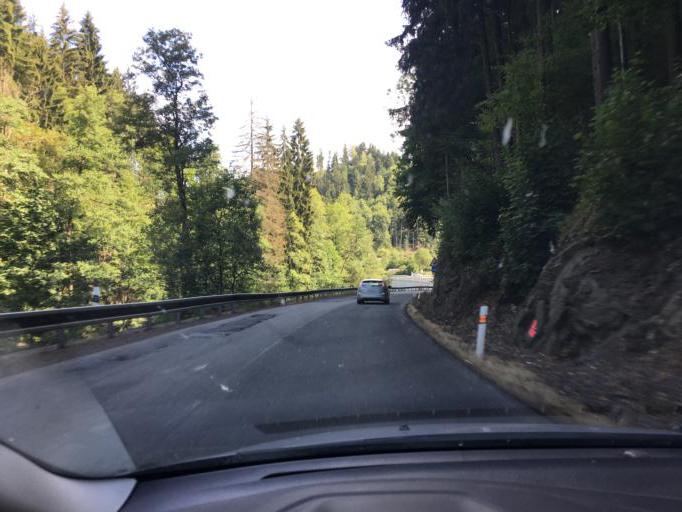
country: CZ
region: Liberecky
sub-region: Okres Semily
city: Ponikla
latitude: 50.6404
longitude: 15.4603
